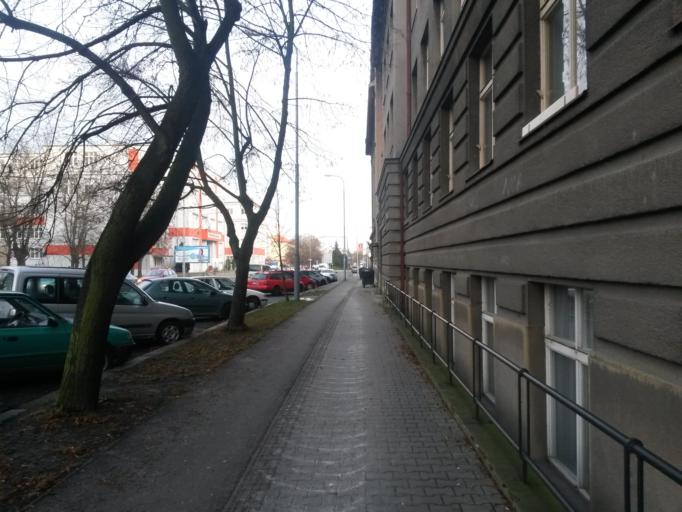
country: CZ
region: Plzensky
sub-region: Okres Plzen-Mesto
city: Pilsen
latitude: 49.7302
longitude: 13.3705
